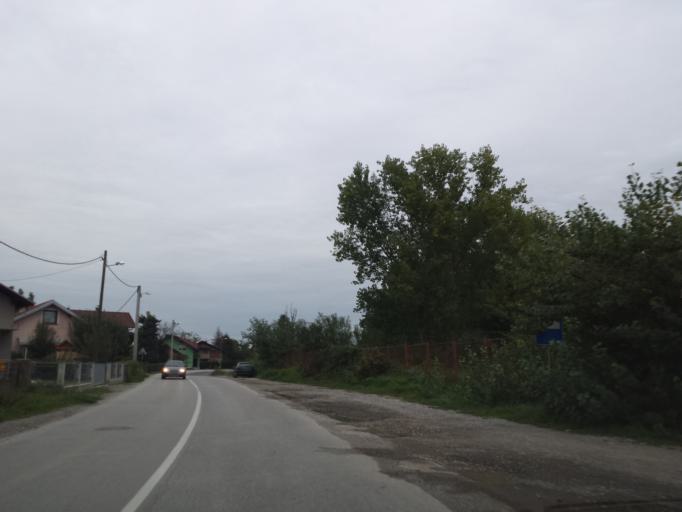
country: HR
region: Grad Zagreb
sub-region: Sesvete
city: Sesvete
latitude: 45.7903
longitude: 16.1366
